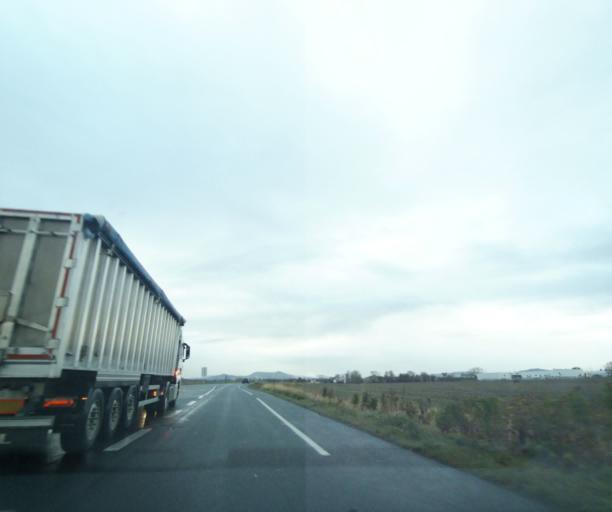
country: FR
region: Auvergne
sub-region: Departement du Puy-de-Dome
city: Perignat-les-Sarlieve
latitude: 45.7608
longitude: 3.1517
